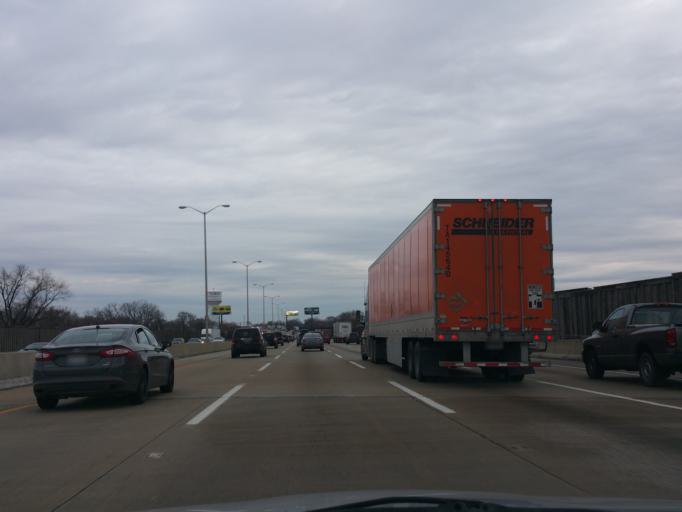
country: US
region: Illinois
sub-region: Cook County
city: Chicago Ridge
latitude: 41.6978
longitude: -87.7859
